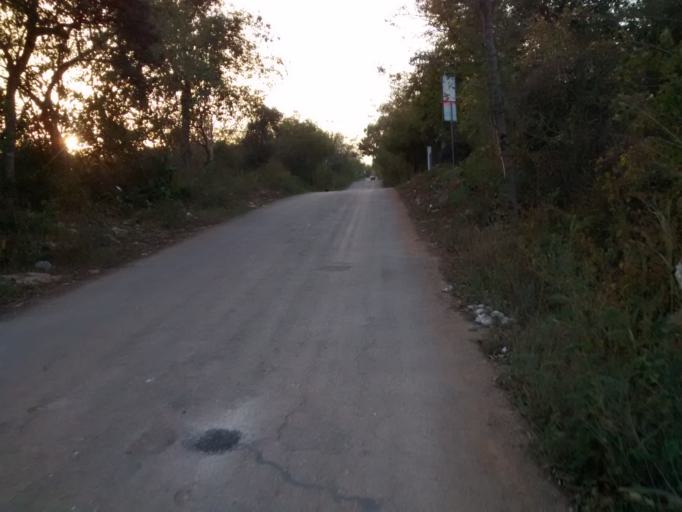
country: MX
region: Yucatan
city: Valladolid
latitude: 20.6837
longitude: -88.1751
